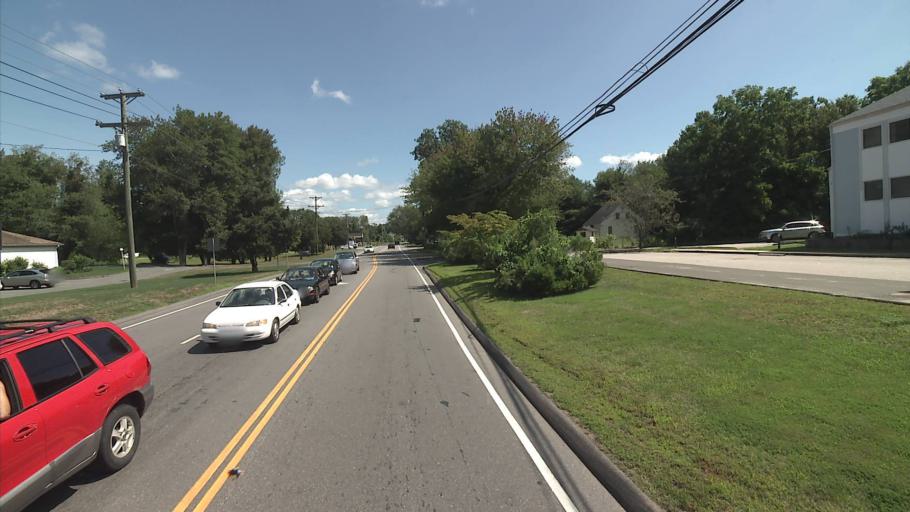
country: US
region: Connecticut
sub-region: Middlesex County
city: Old Saybrook Center
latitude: 41.3223
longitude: -72.3399
